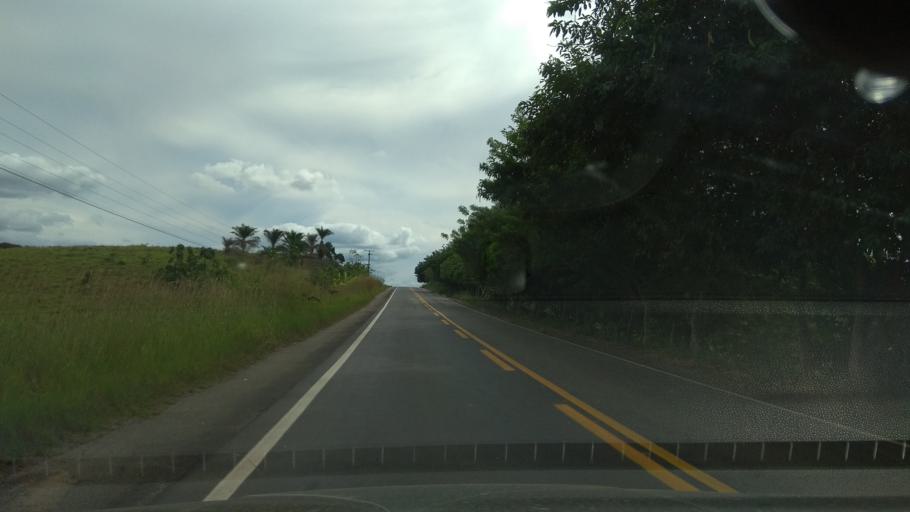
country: BR
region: Bahia
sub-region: Ubata
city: Ubata
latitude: -14.1968
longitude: -39.6224
